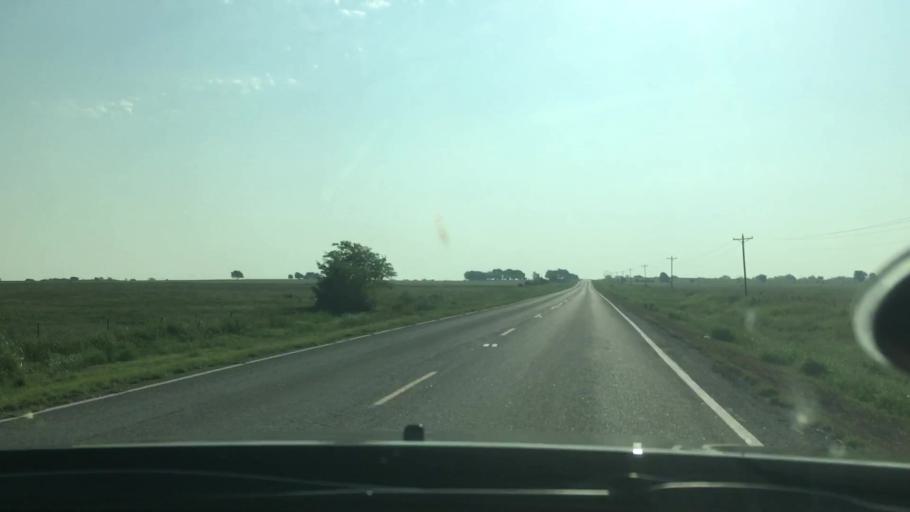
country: US
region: Oklahoma
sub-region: Bryan County
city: Durant
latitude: 34.1427
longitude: -96.3334
